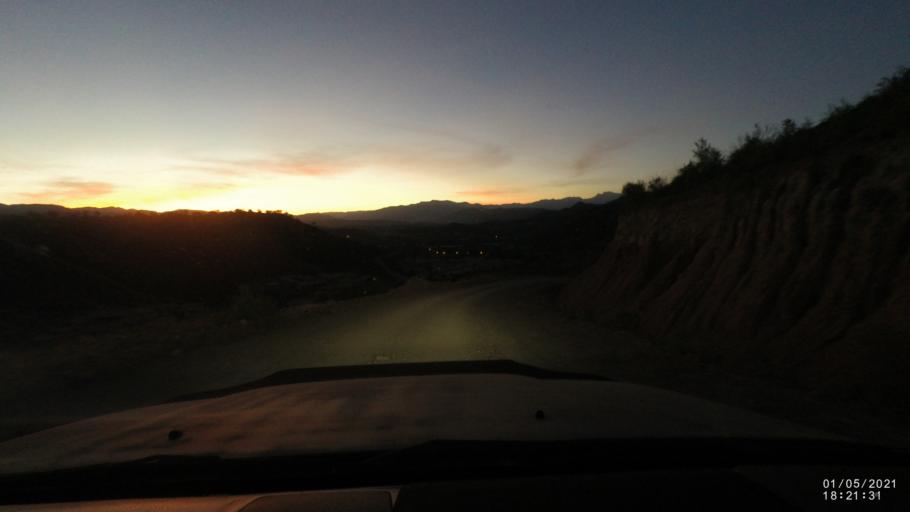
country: BO
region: Cochabamba
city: Capinota
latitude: -17.6623
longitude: -66.2304
